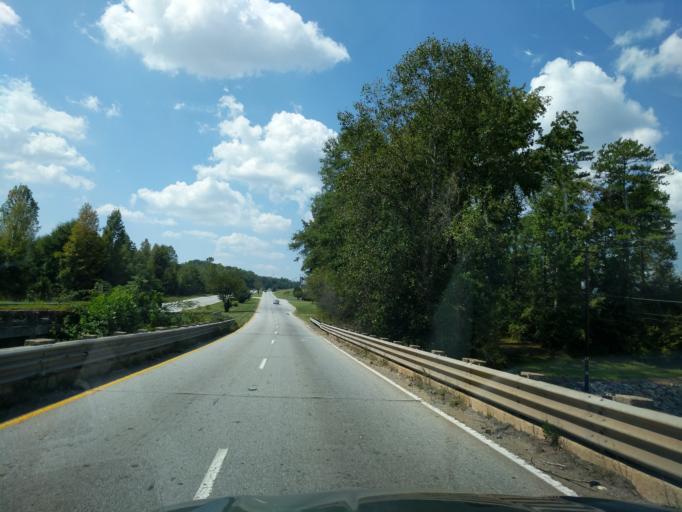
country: US
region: South Carolina
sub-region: Spartanburg County
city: Fairforest
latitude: 34.9398
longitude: -82.0542
